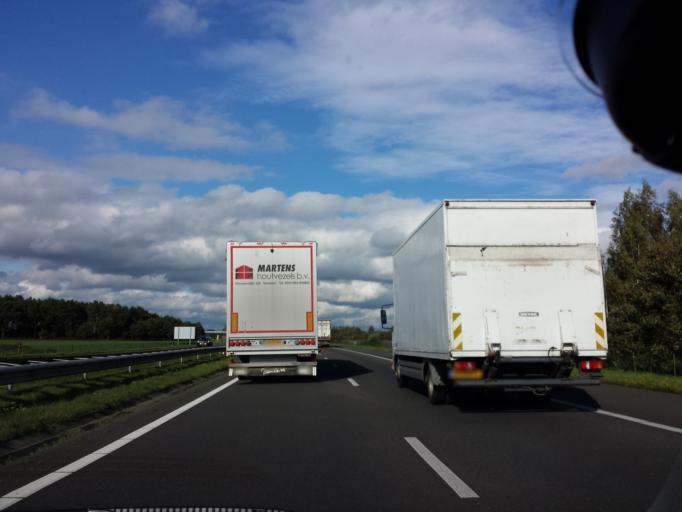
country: NL
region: North Brabant
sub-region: Gemeente Boxmeer
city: Overloon
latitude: 51.5953
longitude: 5.9734
